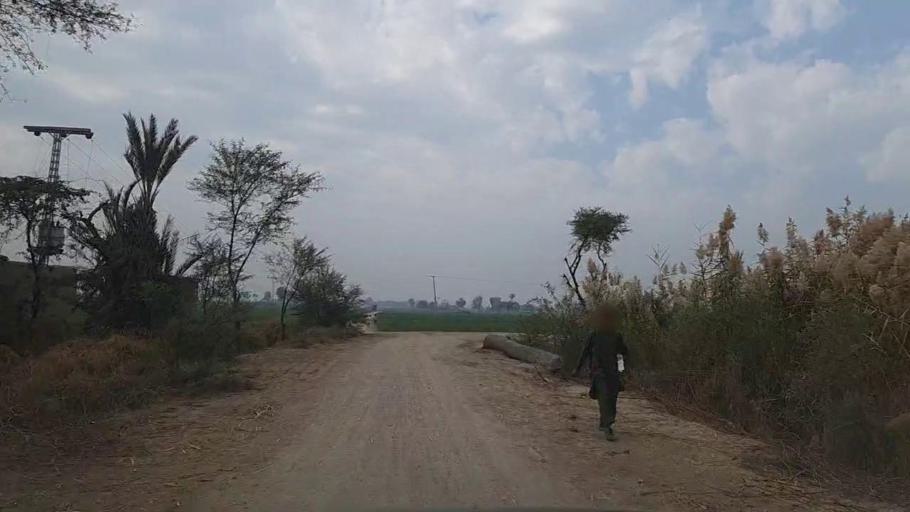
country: PK
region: Sindh
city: Daur
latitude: 26.3610
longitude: 68.3798
